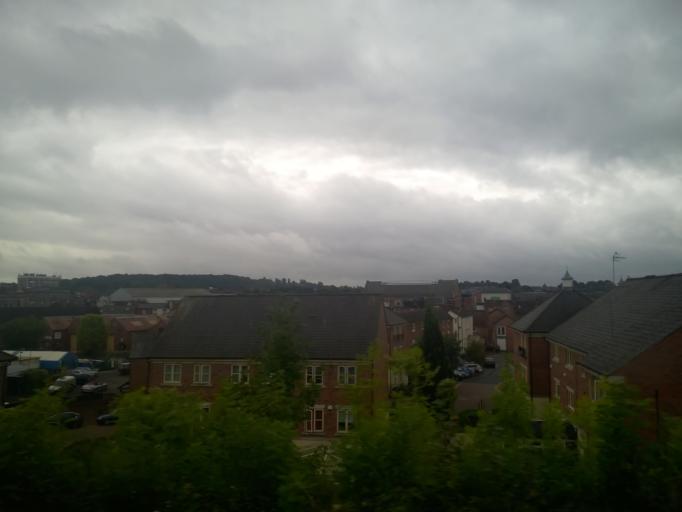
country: GB
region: England
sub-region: Worcestershire
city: Worcester
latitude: 52.1961
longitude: -2.2188
